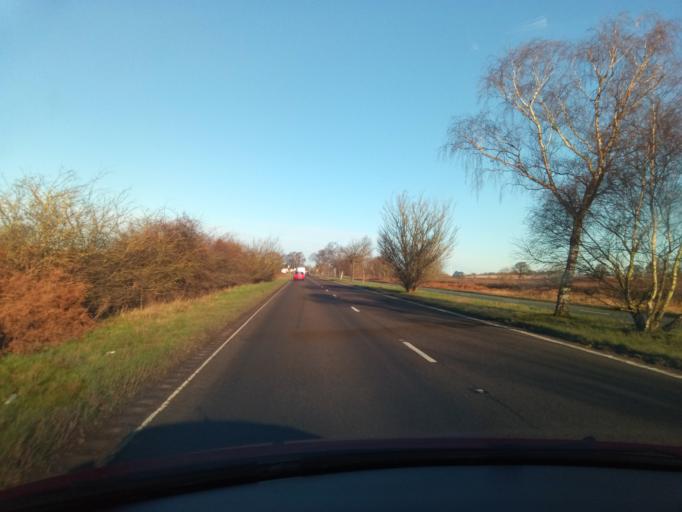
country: GB
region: England
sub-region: Nottinghamshire
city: Farnsfield
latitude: 53.0646
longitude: -1.0707
